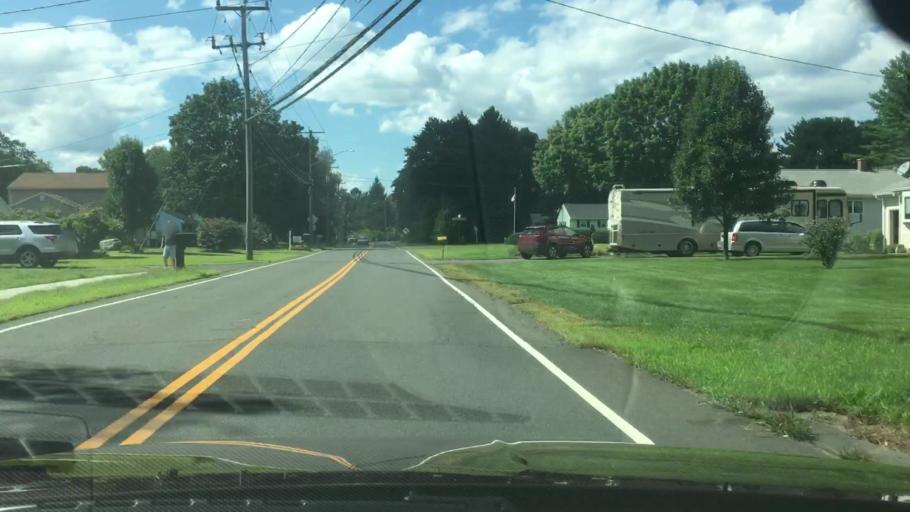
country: US
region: Connecticut
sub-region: Tolland County
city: Rockville
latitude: 41.8662
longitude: -72.4867
